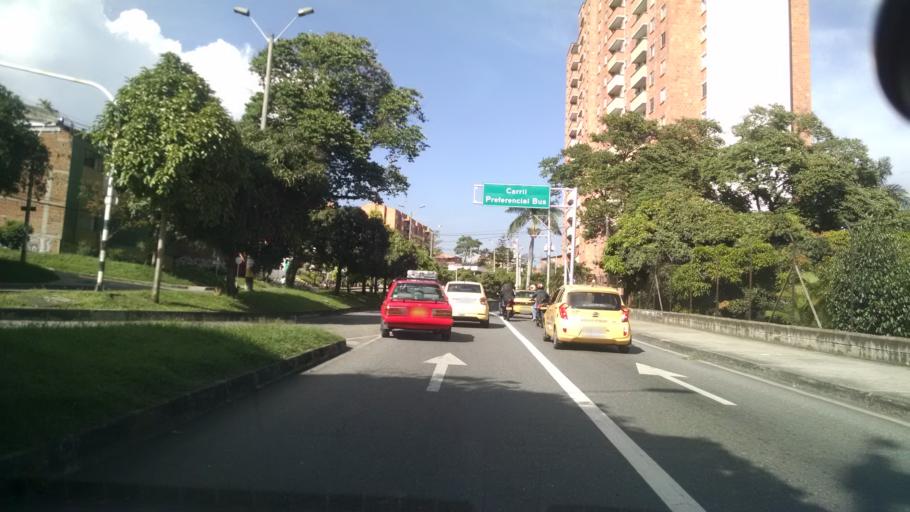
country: CO
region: Antioquia
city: Medellin
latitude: 6.2775
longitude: -75.5892
